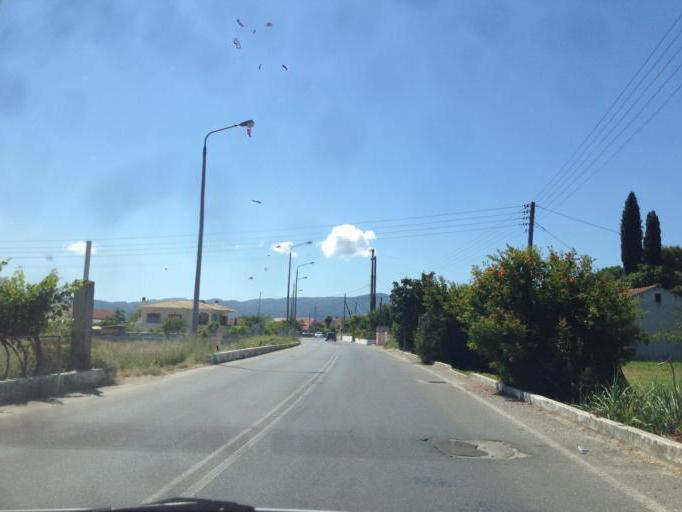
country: GR
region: Ionian Islands
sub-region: Nomos Kerkyras
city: Agios Georgis
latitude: 39.7723
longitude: 19.7127
